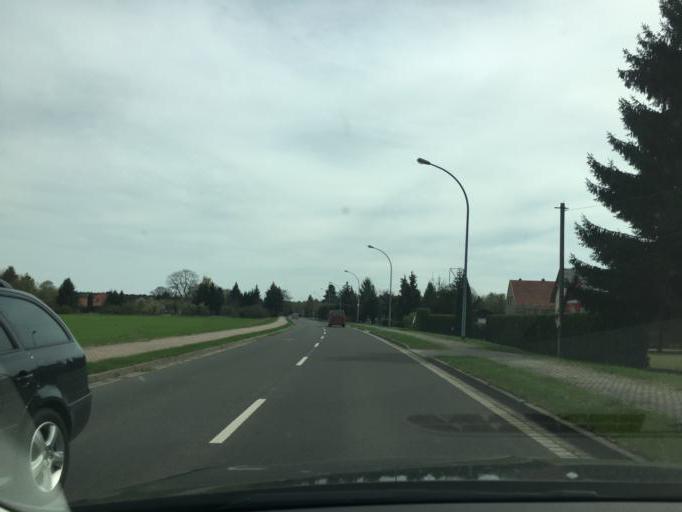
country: DE
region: Saxony
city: Schleife
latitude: 51.5728
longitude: 14.4938
